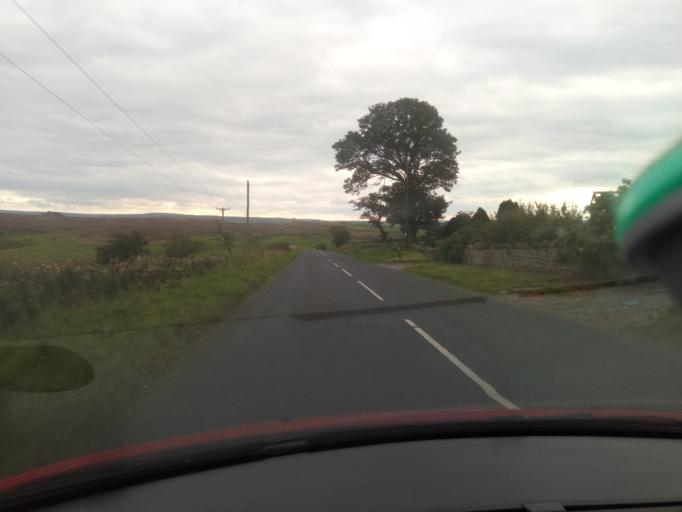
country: GB
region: England
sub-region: Northumberland
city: Bardon Mill
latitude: 54.9395
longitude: -2.2457
